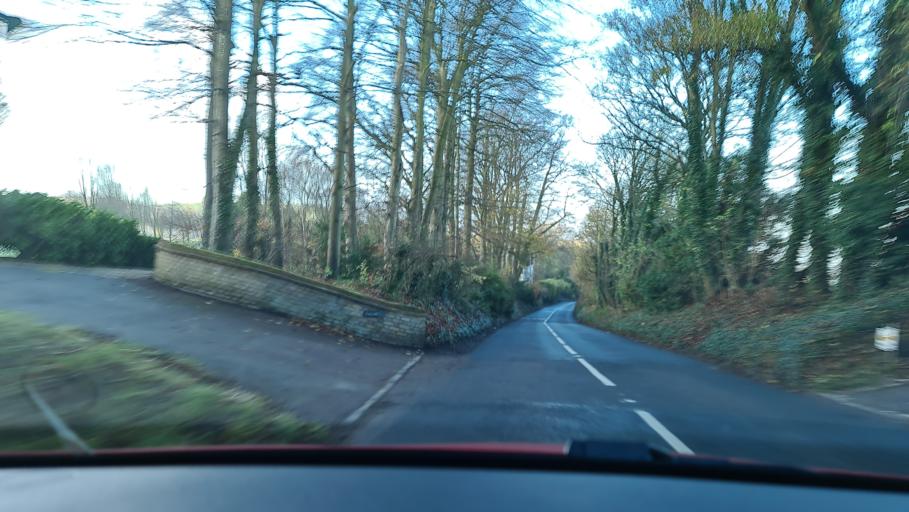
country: GB
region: England
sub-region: Buckinghamshire
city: Wendover
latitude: 51.7564
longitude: -0.7740
